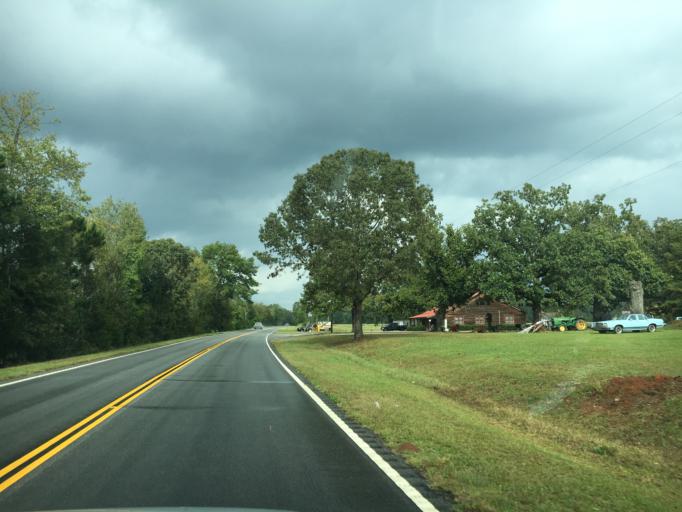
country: US
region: Georgia
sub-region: Hart County
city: Reed Creek
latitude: 34.3998
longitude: -82.8046
